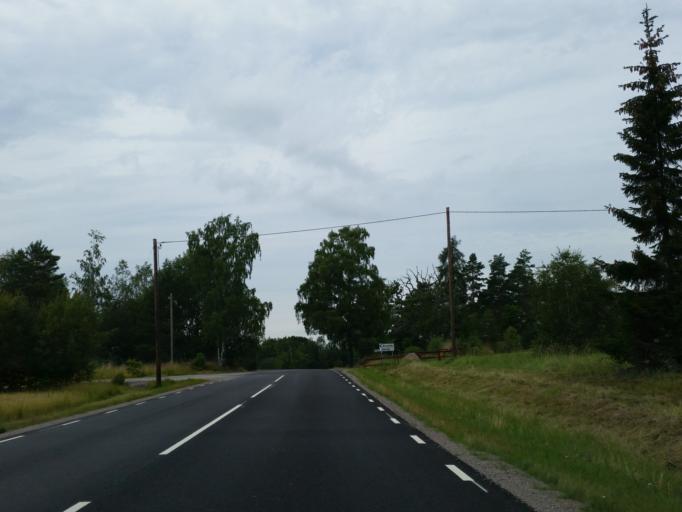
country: SE
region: Soedermanland
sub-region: Strangnas Kommun
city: Mariefred
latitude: 59.2707
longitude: 17.1524
